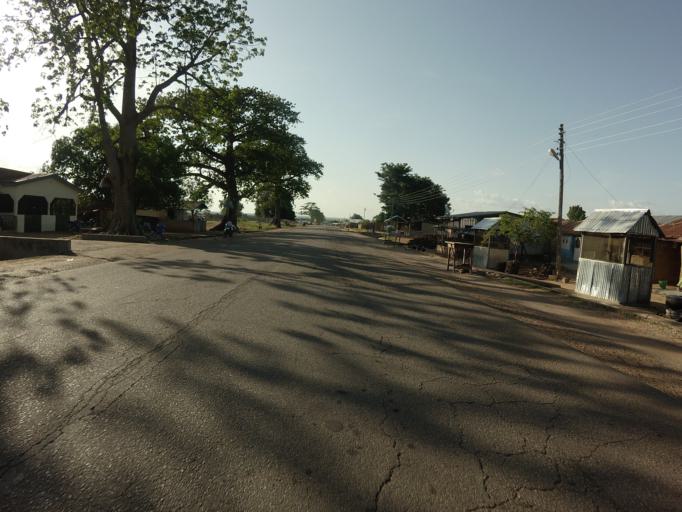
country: GH
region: Upper East
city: Navrongo
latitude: 10.9767
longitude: -1.1048
